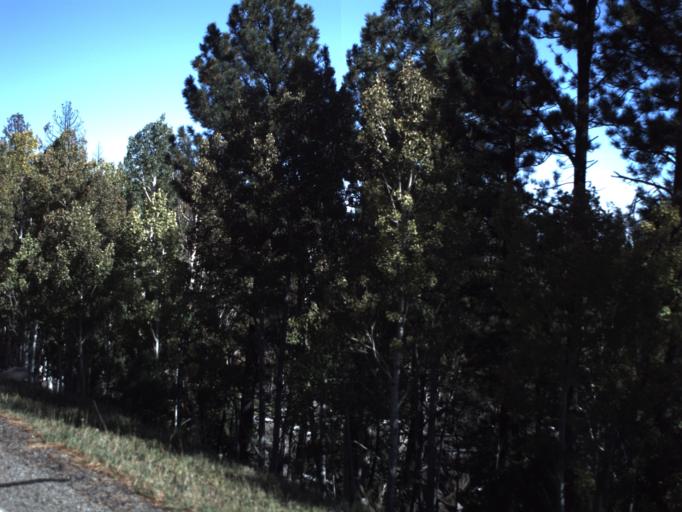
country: US
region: Utah
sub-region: Iron County
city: Parowan
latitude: 37.6546
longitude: -112.6744
